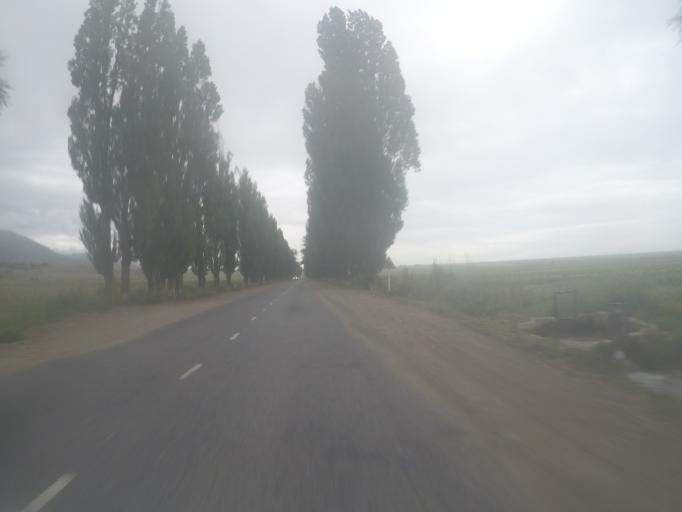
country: KG
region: Ysyk-Koel
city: Cholpon-Ata
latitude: 42.6933
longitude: 77.3822
